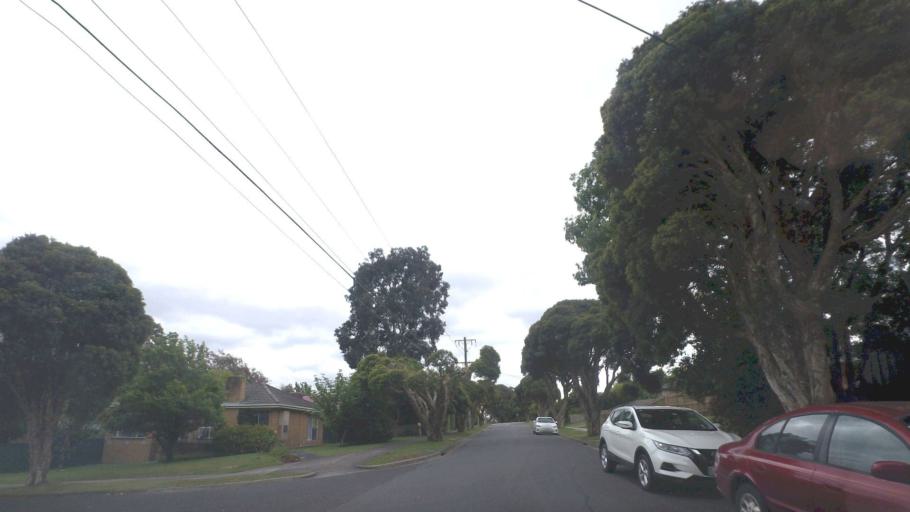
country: AU
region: Victoria
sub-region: Maroondah
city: Croydon South
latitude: -37.8138
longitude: 145.2822
